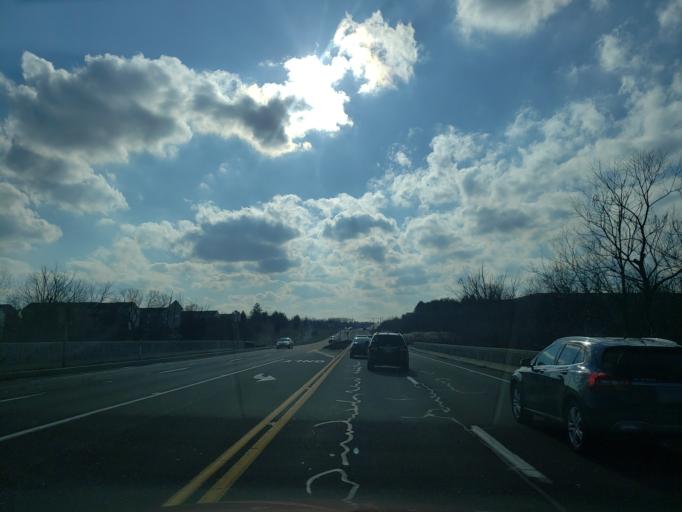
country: US
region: Pennsylvania
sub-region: Montgomery County
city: Montgomeryville
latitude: 40.2381
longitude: -75.2305
